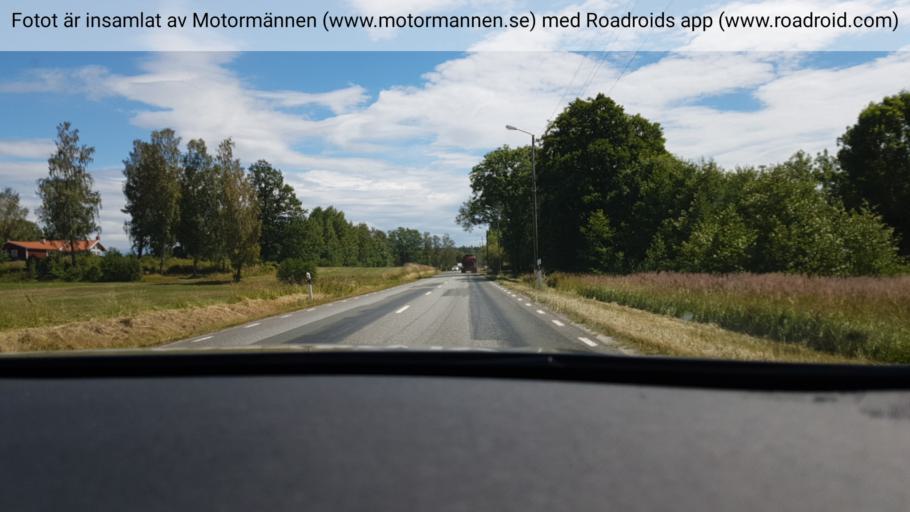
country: SE
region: Joenkoeping
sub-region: Jonkopings Kommun
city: Asa
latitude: 58.0009
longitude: 14.7249
